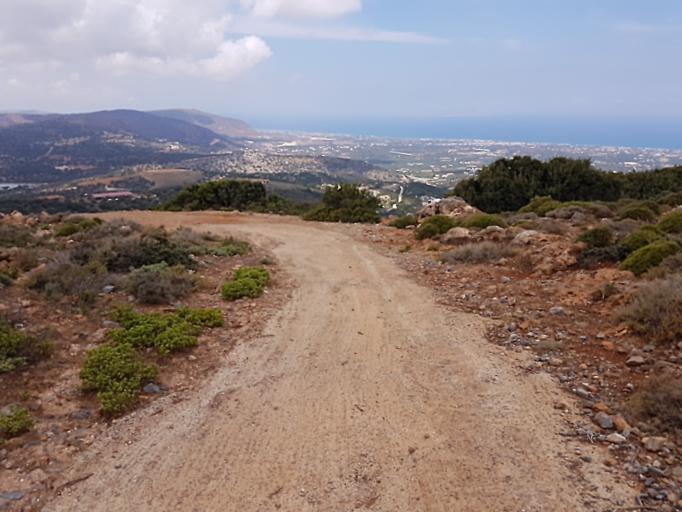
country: GR
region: Crete
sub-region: Nomos Irakleiou
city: Limin Khersonisou
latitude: 35.2922
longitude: 25.3780
